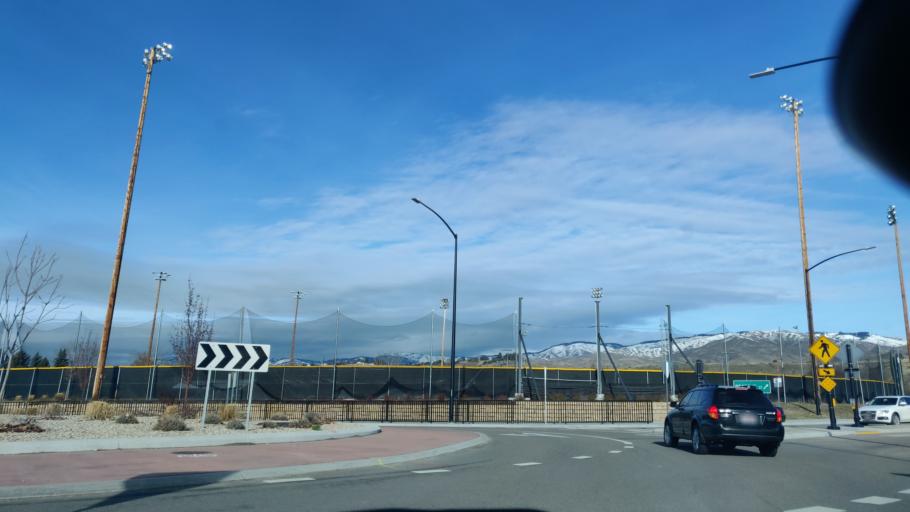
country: US
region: Idaho
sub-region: Ada County
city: Boise
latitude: 43.6134
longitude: -116.1906
